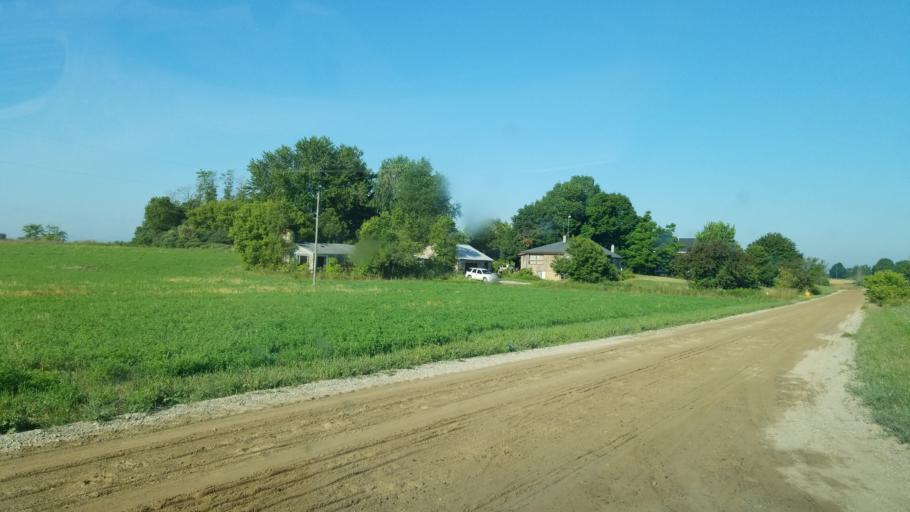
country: US
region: Michigan
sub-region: Mecosta County
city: Canadian Lakes
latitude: 43.5545
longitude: -85.3537
